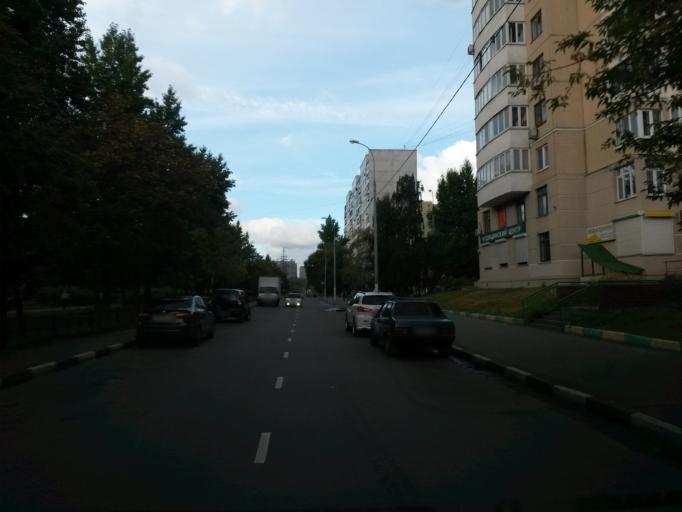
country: RU
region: Moscow
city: Mar'ino
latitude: 55.6493
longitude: 37.7144
